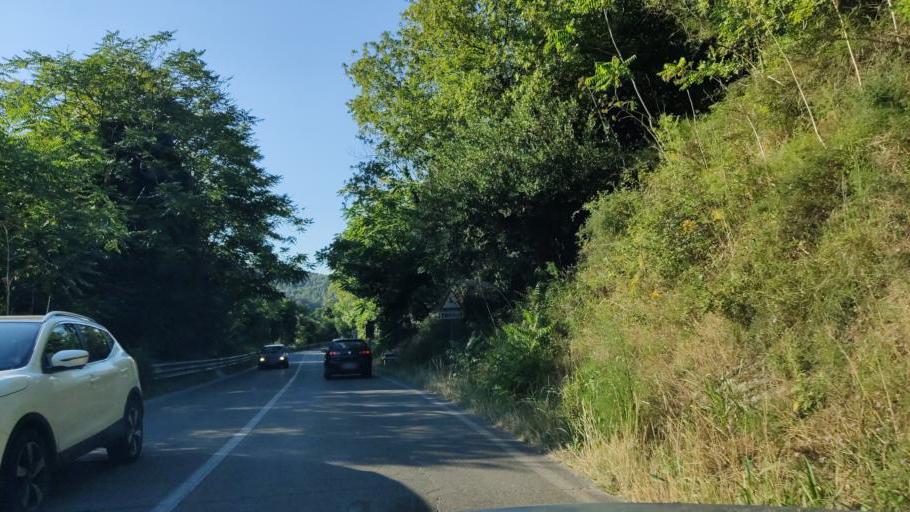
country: IT
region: Umbria
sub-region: Provincia di Terni
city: Narni
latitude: 42.5173
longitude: 12.5129
